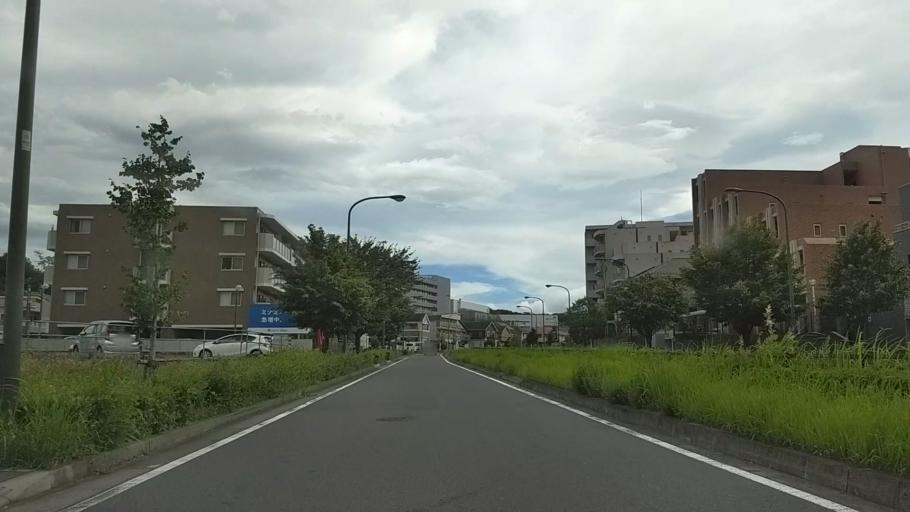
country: JP
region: Tokyo
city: Hachioji
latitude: 35.6255
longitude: 139.3276
